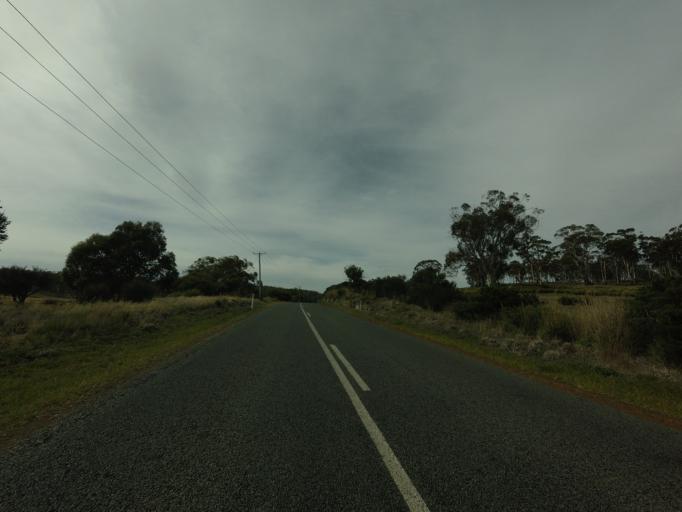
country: AU
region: Tasmania
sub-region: Brighton
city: Bridgewater
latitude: -42.3252
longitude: 147.3898
